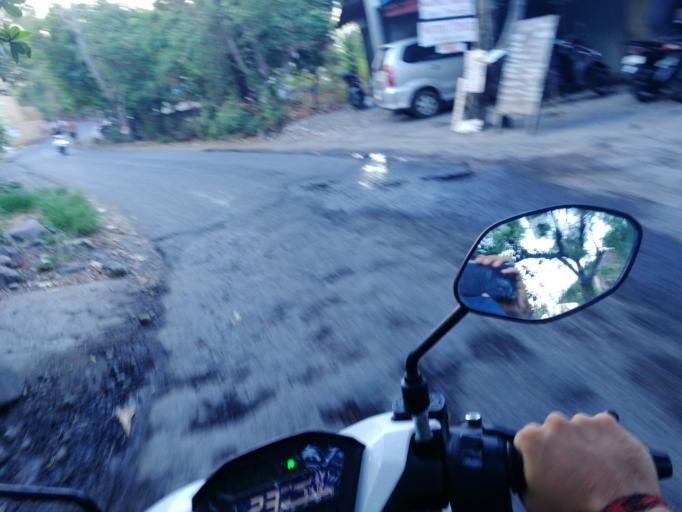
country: ID
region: Bali
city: Biaslantang Kaler
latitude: -8.3364
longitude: 115.6582
